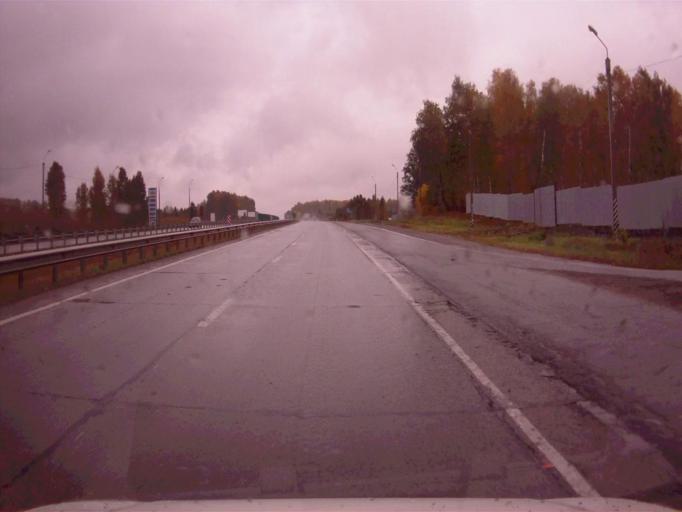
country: RU
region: Chelyabinsk
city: Dolgoderevenskoye
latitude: 55.3267
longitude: 61.3275
